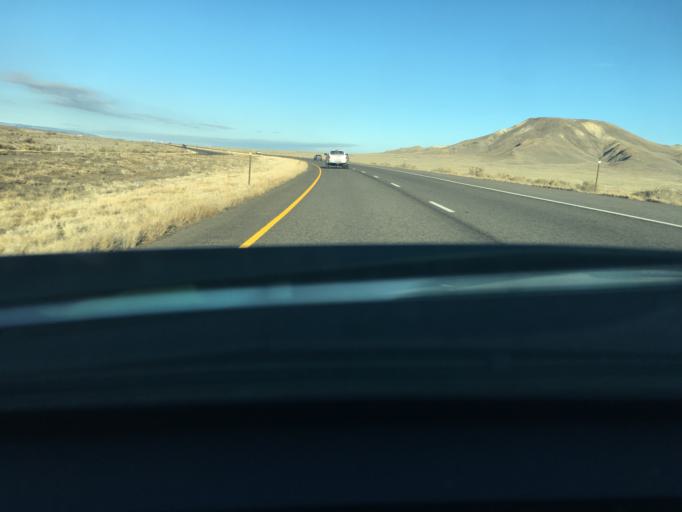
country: US
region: Colorado
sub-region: Delta County
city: Delta
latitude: 38.7758
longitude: -108.2306
